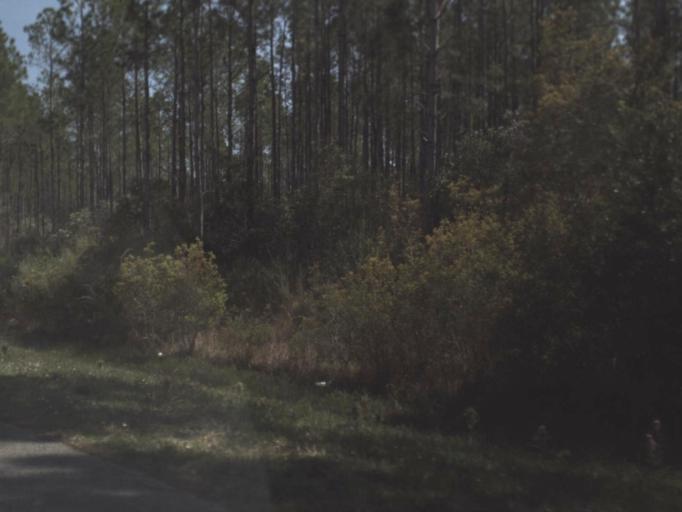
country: US
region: Florida
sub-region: Franklin County
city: Apalachicola
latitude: 29.7322
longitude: -85.1447
